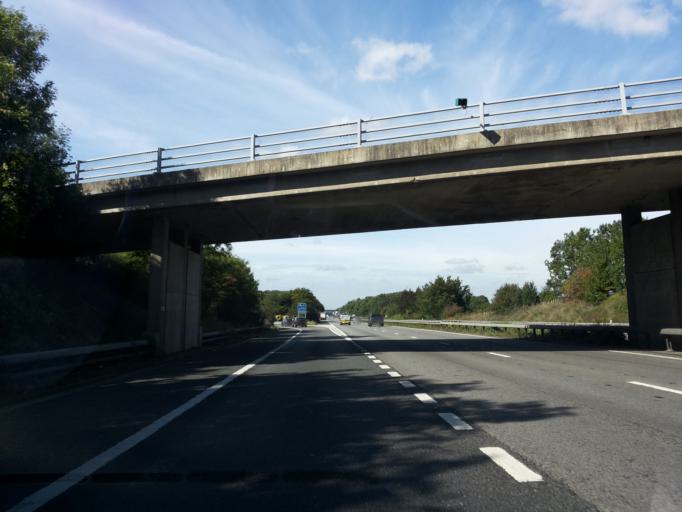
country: GB
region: England
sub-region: Kent
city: Newington
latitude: 51.3274
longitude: 0.6688
